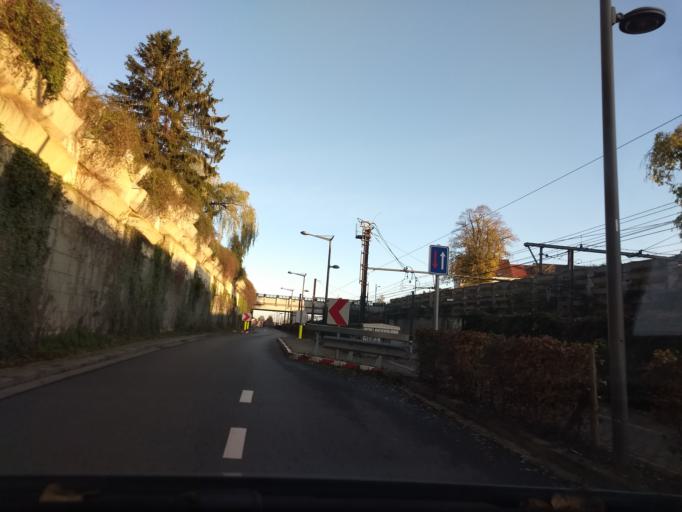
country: BE
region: Wallonia
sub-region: Province du Brabant Wallon
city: Braine-l'Alleud
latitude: 50.6781
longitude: 4.3746
